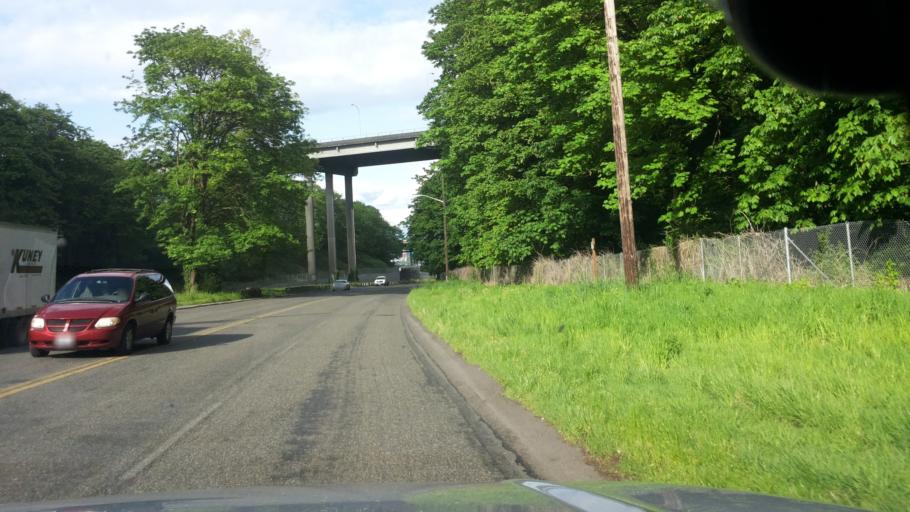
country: US
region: Washington
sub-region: Pierce County
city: Tacoma
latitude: 47.2324
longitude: -122.4449
